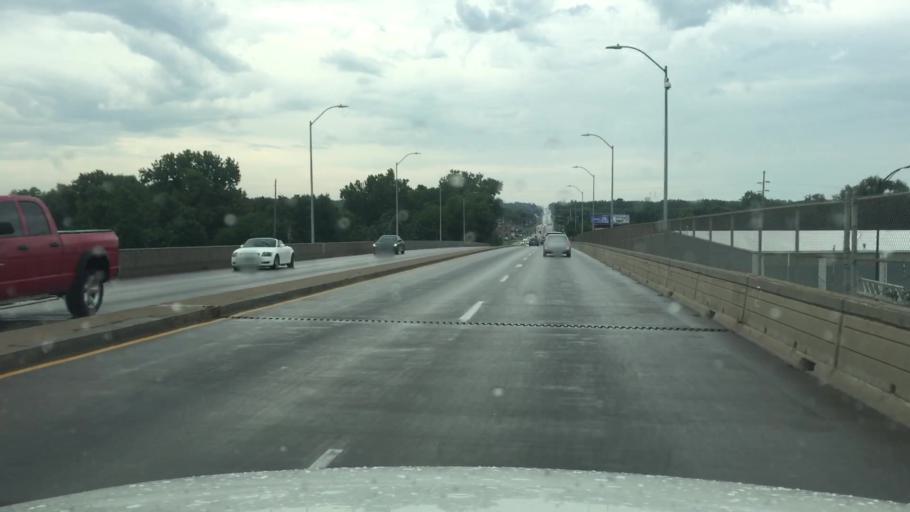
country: US
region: Iowa
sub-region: Polk County
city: Des Moines
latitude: 41.5852
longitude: -93.5970
